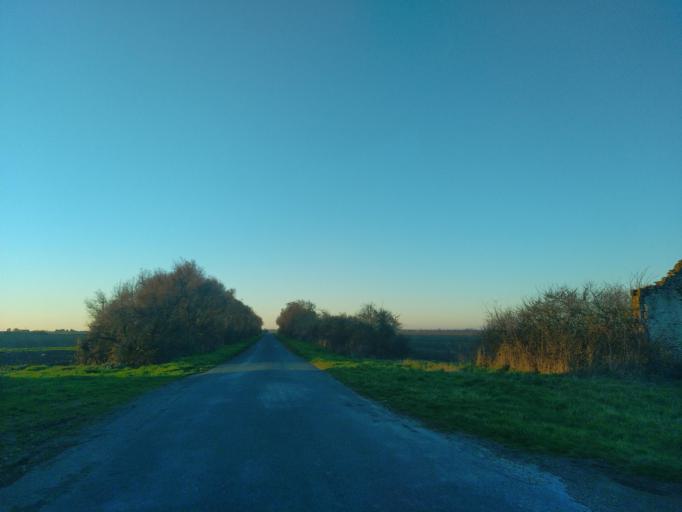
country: FR
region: Pays de la Loire
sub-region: Departement de la Vendee
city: Triaize
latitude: 46.3760
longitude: -1.2920
